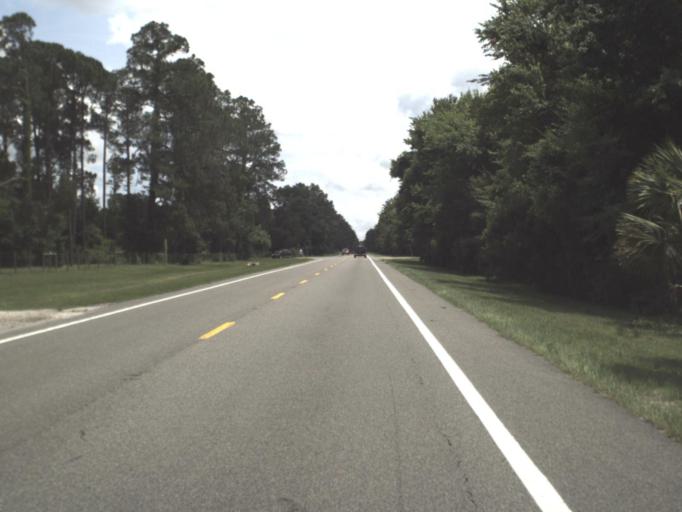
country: US
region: Florida
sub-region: Nassau County
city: Yulee
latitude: 30.6728
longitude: -81.6424
